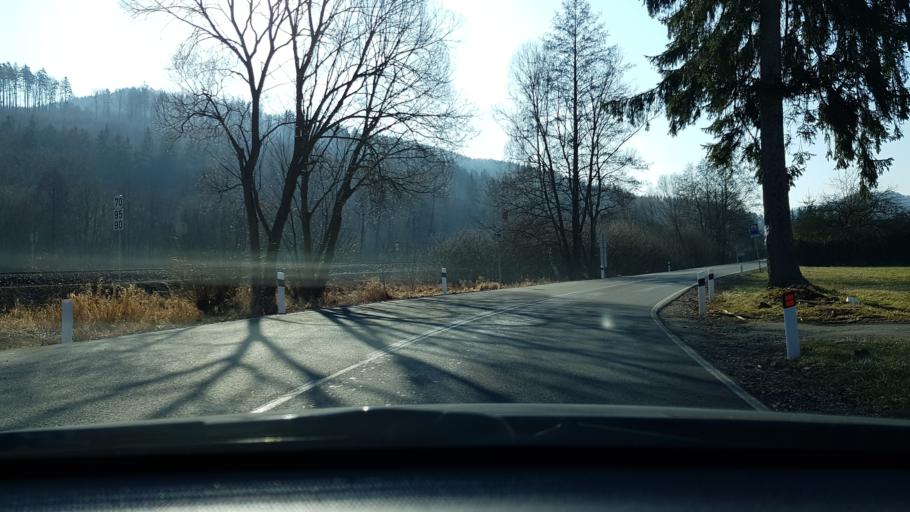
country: CZ
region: Olomoucky
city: Dolni Bohdikov
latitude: 49.9983
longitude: 16.8941
